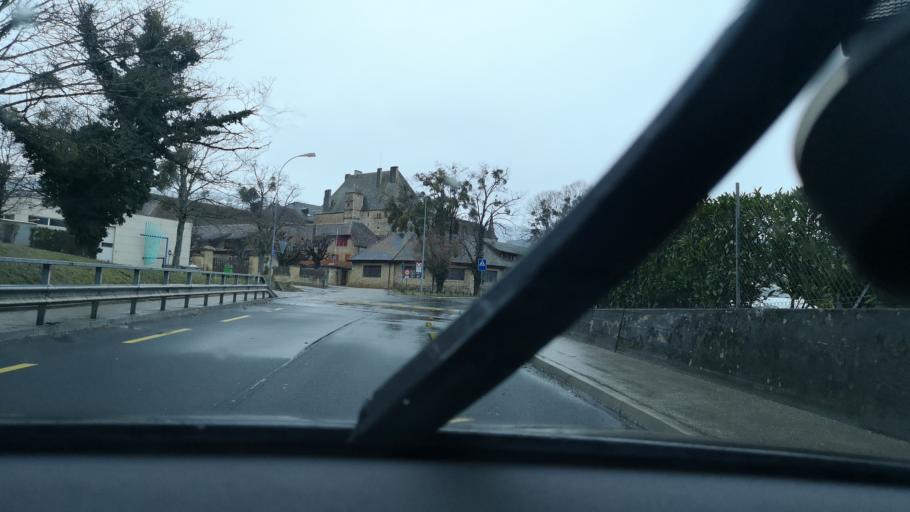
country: CH
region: Neuchatel
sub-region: Boudry District
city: Auvernier
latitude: 46.9644
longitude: 6.8646
